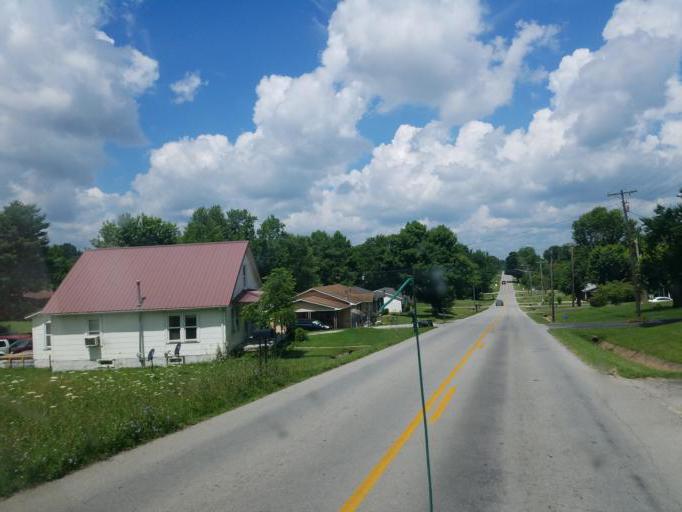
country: US
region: Kentucky
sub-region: Grayson County
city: Leitchfield
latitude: 37.4910
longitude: -86.2951
